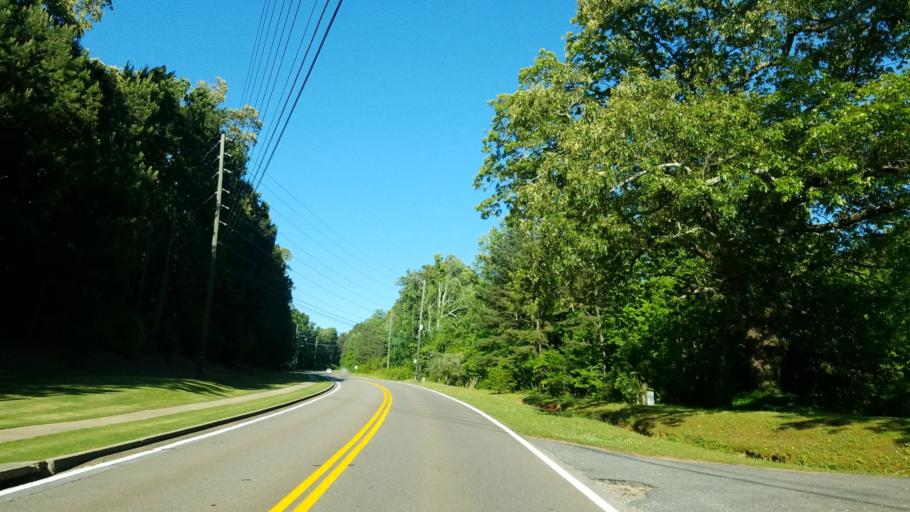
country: US
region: Georgia
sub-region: Cherokee County
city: Holly Springs
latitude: 34.1743
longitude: -84.5220
